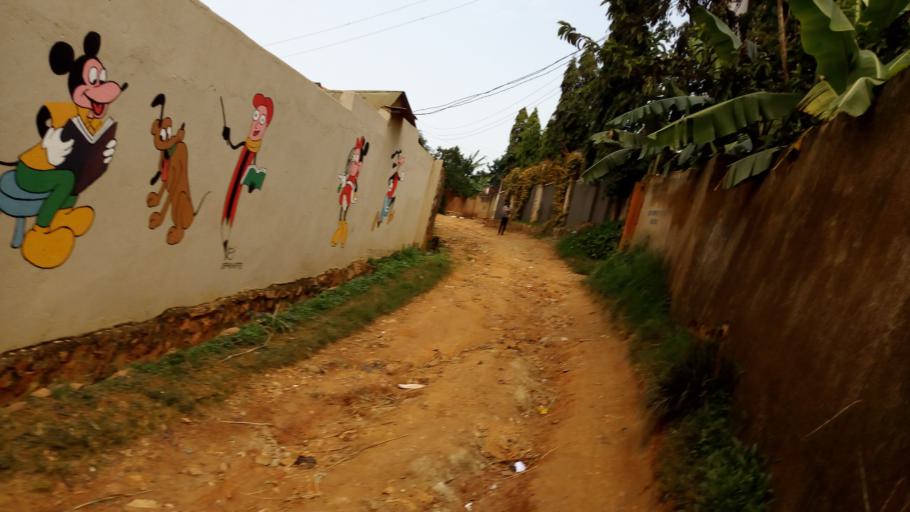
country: UG
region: Central Region
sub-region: Wakiso District
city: Kireka
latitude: 0.3203
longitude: 32.6409
